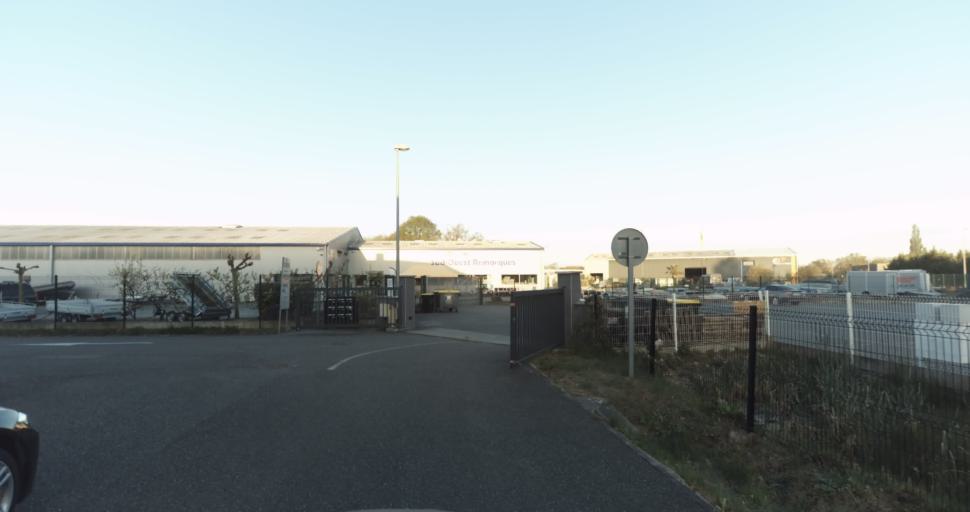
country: FR
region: Aquitaine
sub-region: Departement de la Gironde
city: Martignas-sur-Jalle
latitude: 44.8133
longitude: -0.7463
